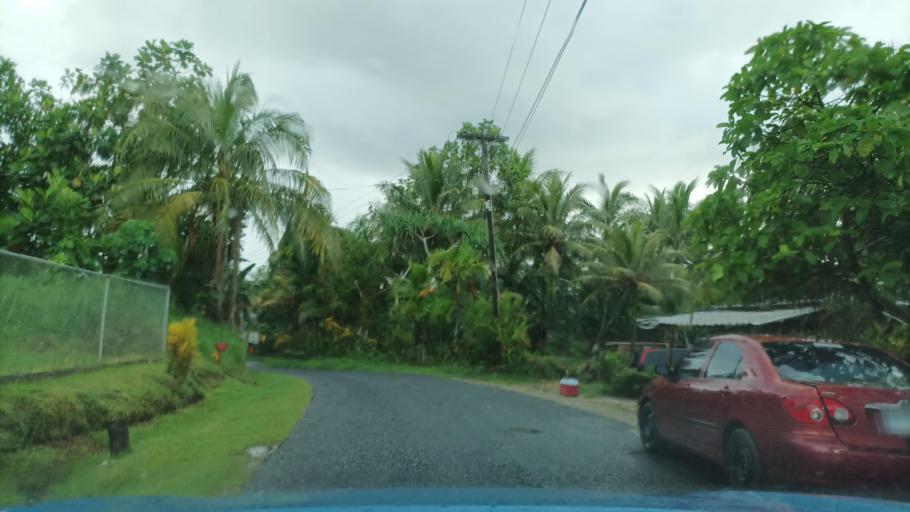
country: FM
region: Pohnpei
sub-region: Sokehs Municipality
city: Palikir - National Government Center
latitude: 6.9213
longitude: 158.1563
